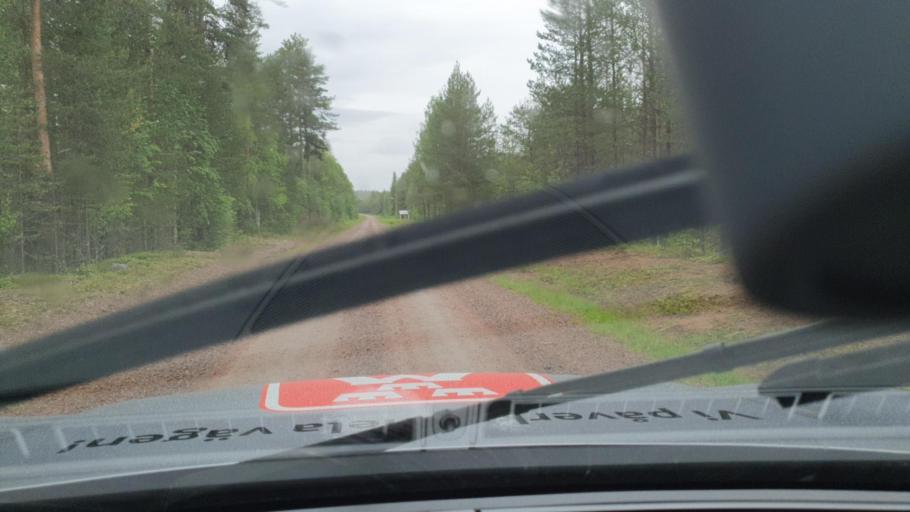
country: SE
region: Norrbotten
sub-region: Overkalix Kommun
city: OEverkalix
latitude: 66.5612
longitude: 22.7480
